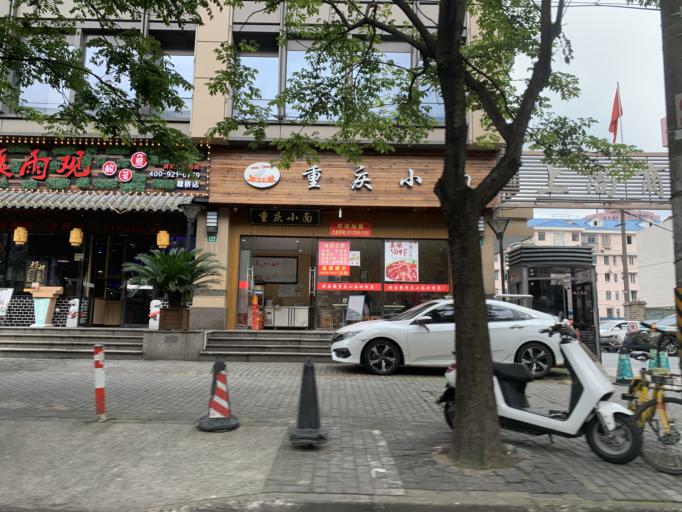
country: CN
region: Shanghai Shi
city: Pudong
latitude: 31.2128
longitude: 121.5118
